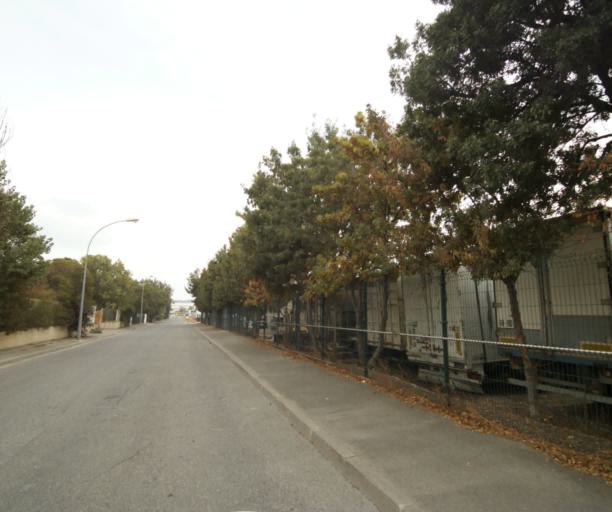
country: FR
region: Provence-Alpes-Cote d'Azur
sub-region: Departement des Bouches-du-Rhone
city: Marignane
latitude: 43.4063
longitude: 5.1992
